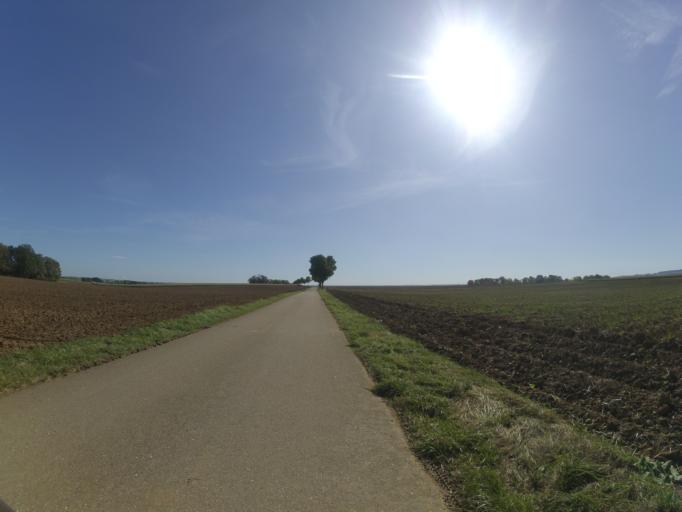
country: DE
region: Baden-Wuerttemberg
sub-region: Tuebingen Region
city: Nerenstetten
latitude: 48.5079
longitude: 10.0864
